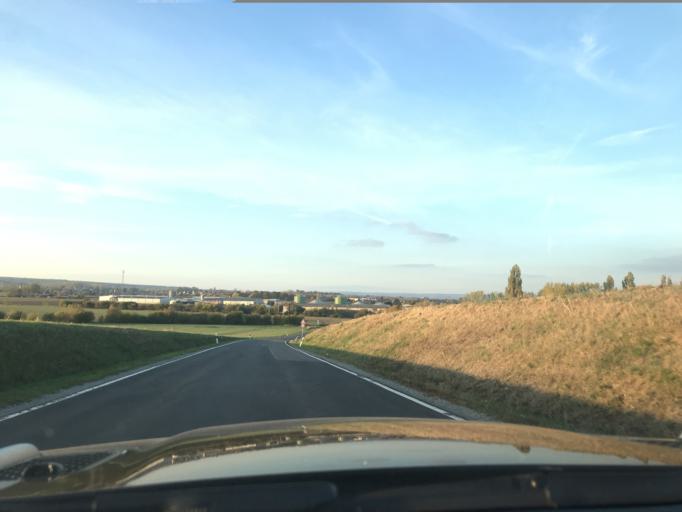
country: DE
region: Thuringia
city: Niederdorla
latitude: 51.1486
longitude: 10.4411
